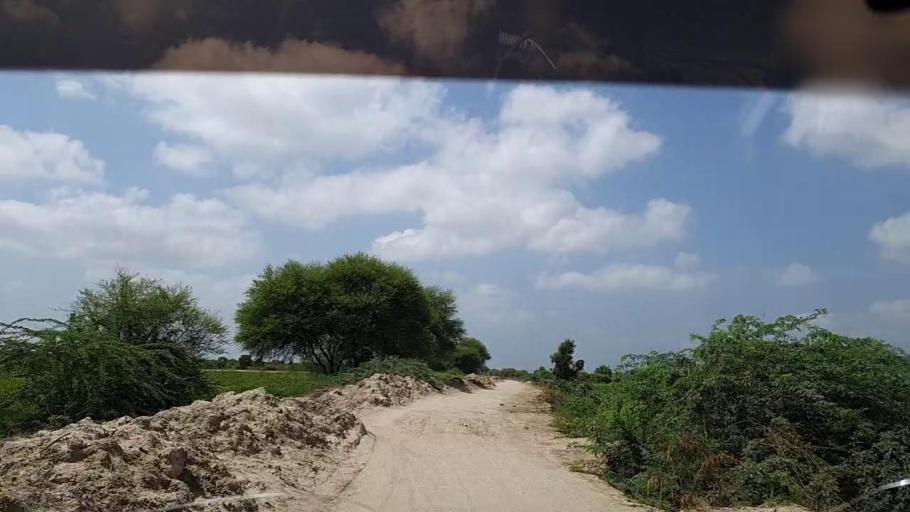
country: PK
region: Sindh
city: Badin
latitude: 24.5969
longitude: 68.7800
